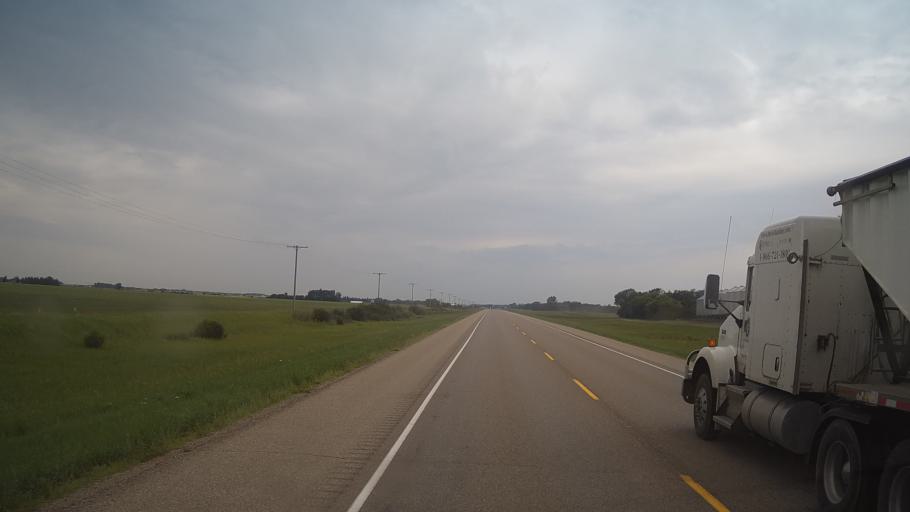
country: CA
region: Saskatchewan
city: Langham
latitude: 52.1289
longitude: -107.1988
